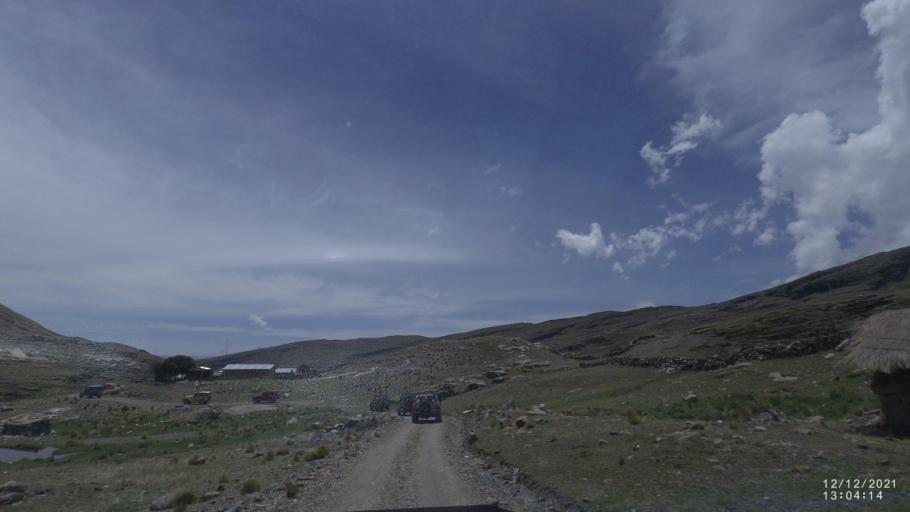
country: BO
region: Cochabamba
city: Cochabamba
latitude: -17.2677
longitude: -66.1682
